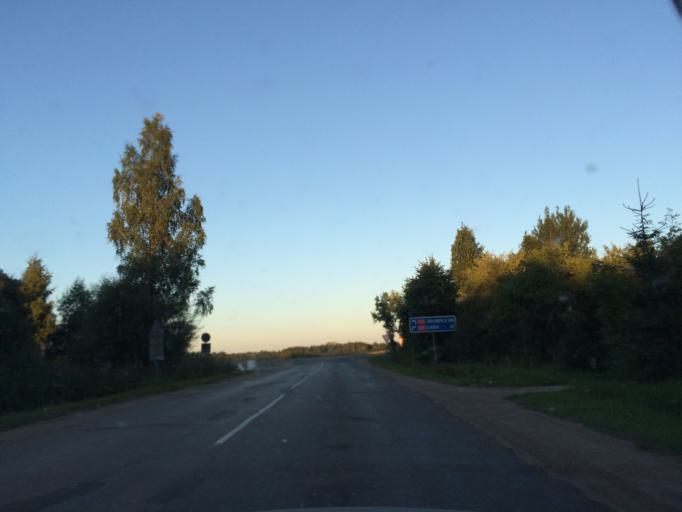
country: LV
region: Rezekne
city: Rezekne
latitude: 56.5150
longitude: 27.4204
